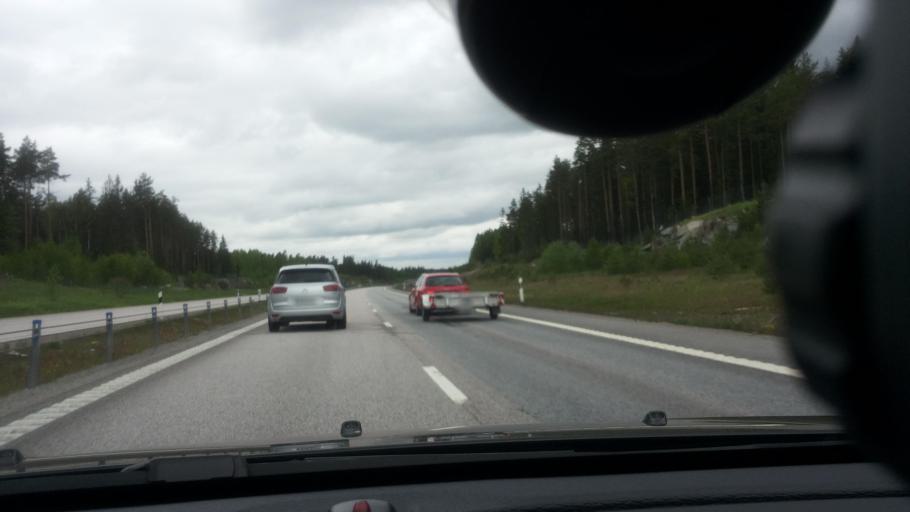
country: SE
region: Uppsala
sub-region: Tierps Kommun
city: Tierp
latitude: 60.1835
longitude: 17.5027
